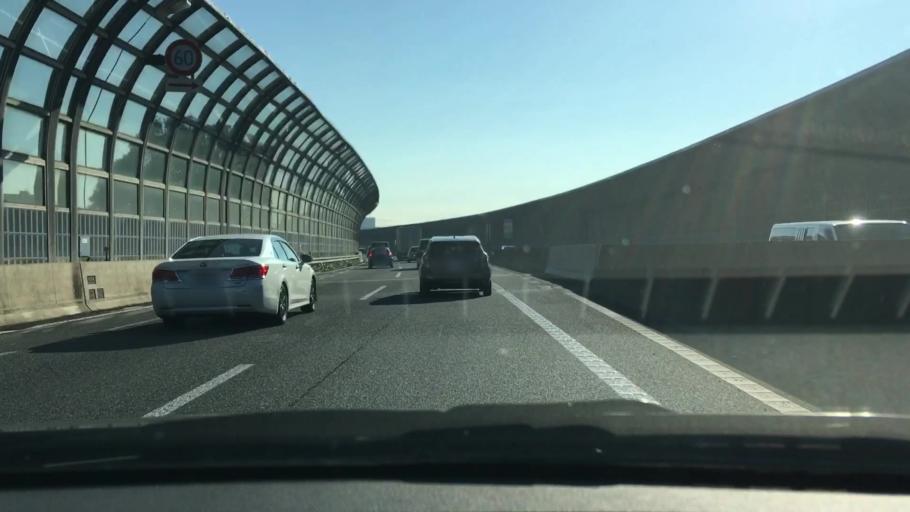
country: JP
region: Chiba
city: Funabashi
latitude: 35.6947
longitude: 139.9762
